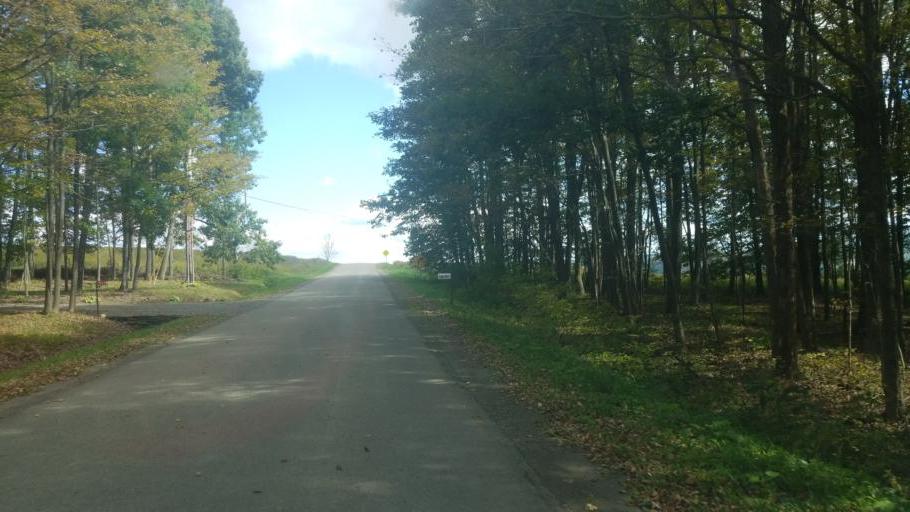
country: US
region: New York
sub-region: Allegany County
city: Cuba
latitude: 42.2005
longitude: -78.3008
